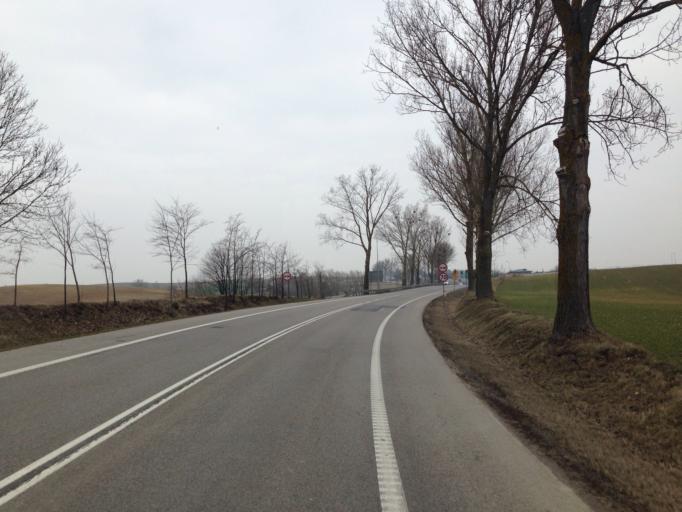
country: PL
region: Pomeranian Voivodeship
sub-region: Powiat tczewski
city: Gniew
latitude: 53.7704
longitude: 18.7691
